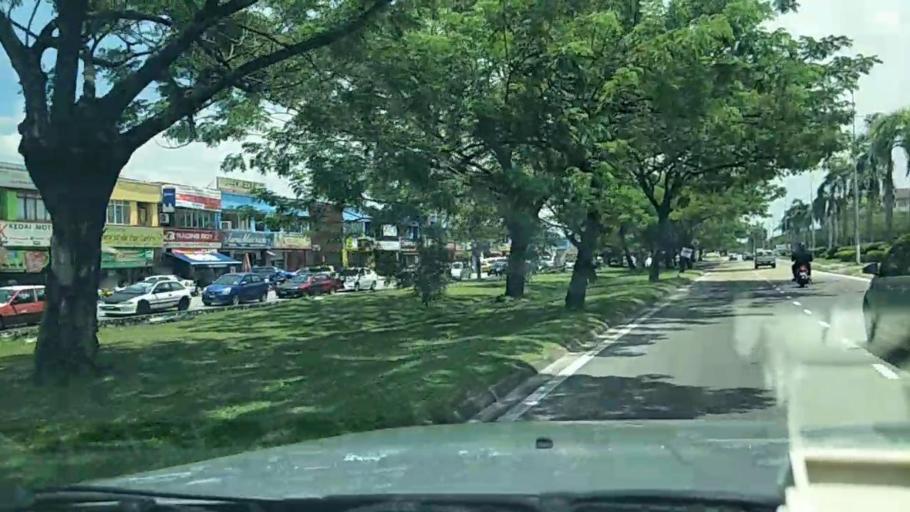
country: MY
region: Putrajaya
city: Putrajaya
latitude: 2.9503
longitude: 101.6170
